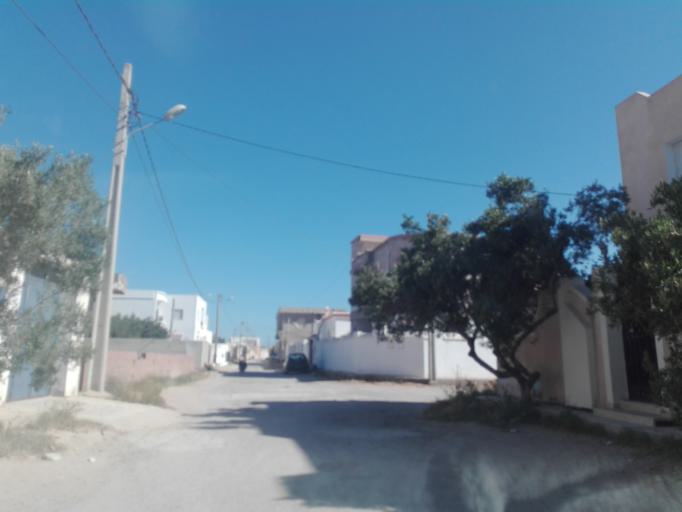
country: TN
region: Safaqis
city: Al Qarmadah
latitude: 34.7105
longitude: 11.2027
